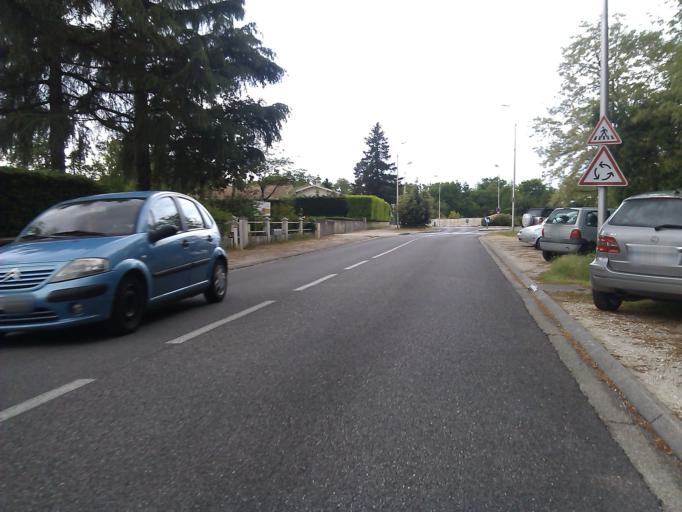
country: FR
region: Aquitaine
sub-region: Departement de la Gironde
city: Cestas
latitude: 44.7464
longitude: -0.6852
